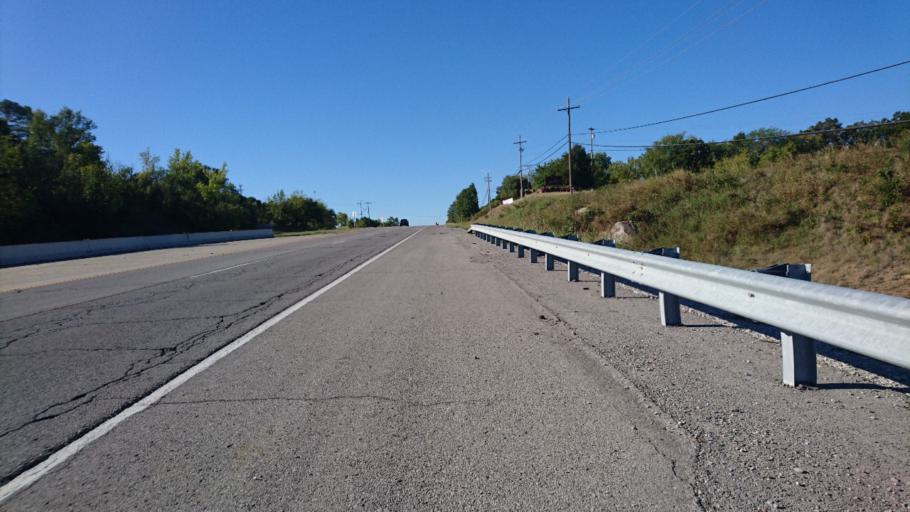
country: US
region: Oklahoma
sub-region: Rogers County
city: Catoosa
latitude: 36.2069
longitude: -95.7258
